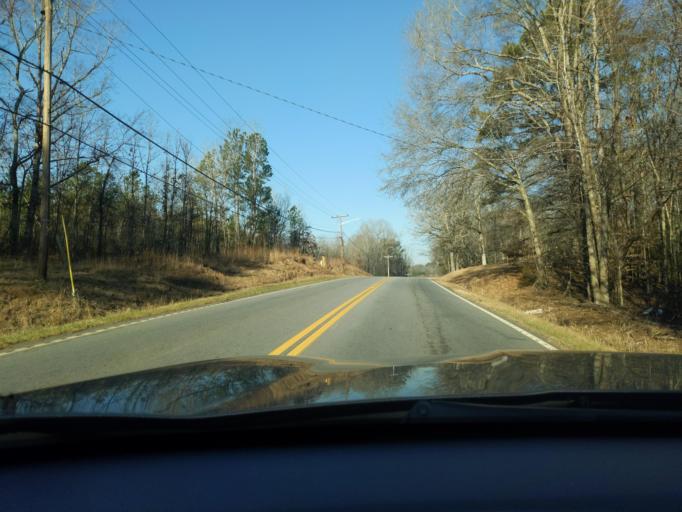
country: US
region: South Carolina
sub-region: Greenwood County
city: Greenwood
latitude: 34.1912
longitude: -82.1223
